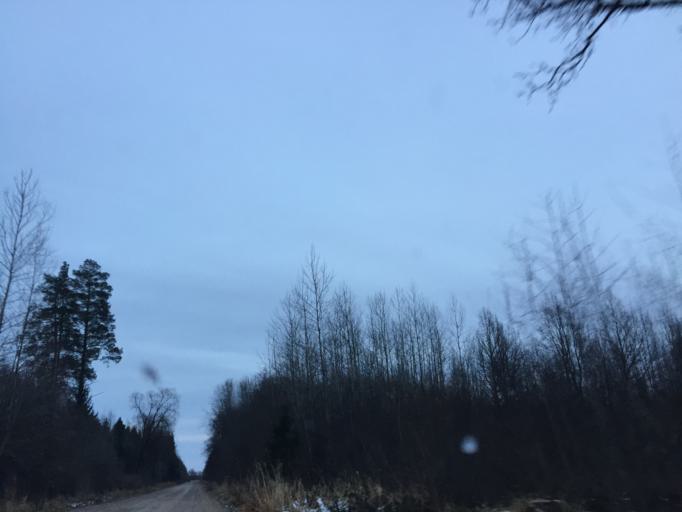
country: LV
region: Burtnieki
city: Matisi
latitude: 57.6298
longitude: 25.1499
